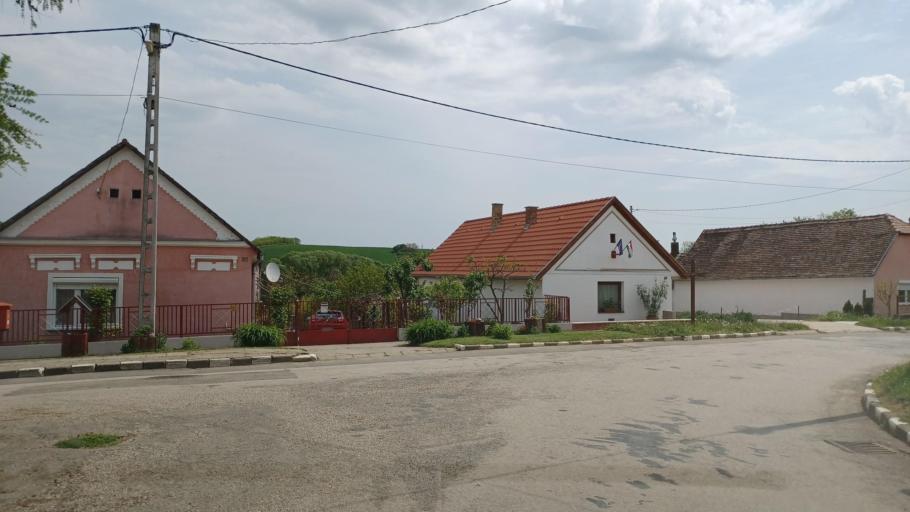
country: HU
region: Baranya
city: Kozarmisleny
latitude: 45.9719
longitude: 18.3608
